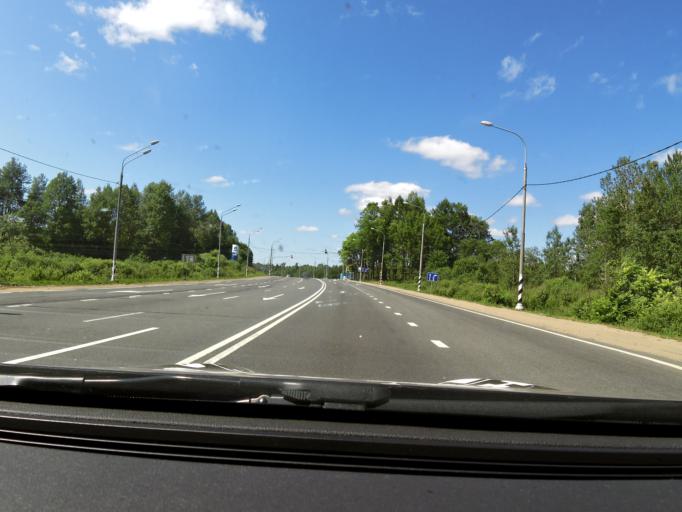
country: RU
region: Novgorod
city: Valday
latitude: 57.9895
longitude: 33.2002
